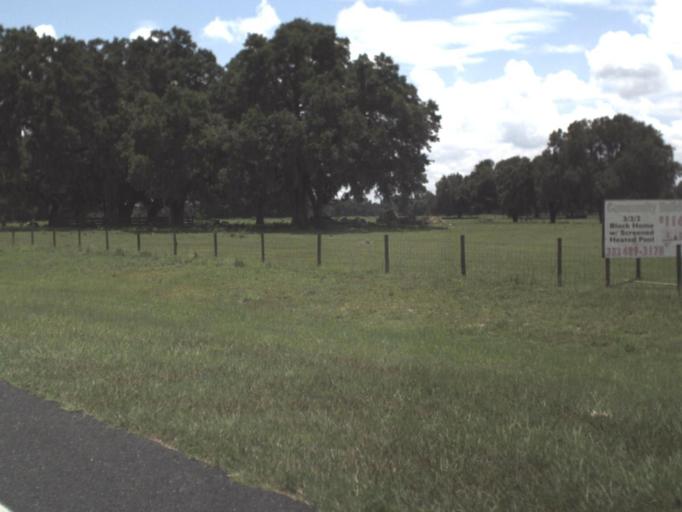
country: US
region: Florida
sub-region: Levy County
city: Williston
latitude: 29.3771
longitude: -82.4195
